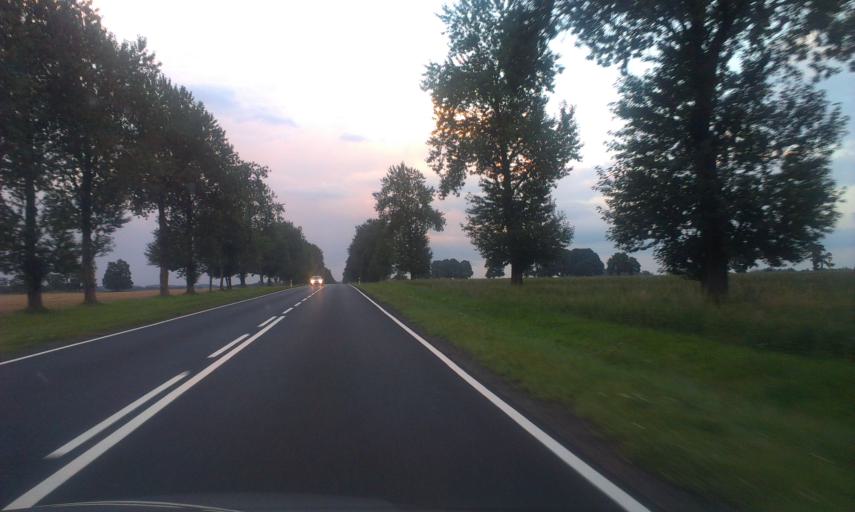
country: PL
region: West Pomeranian Voivodeship
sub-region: Powiat koszalinski
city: Bobolice
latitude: 54.0555
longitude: 16.4218
